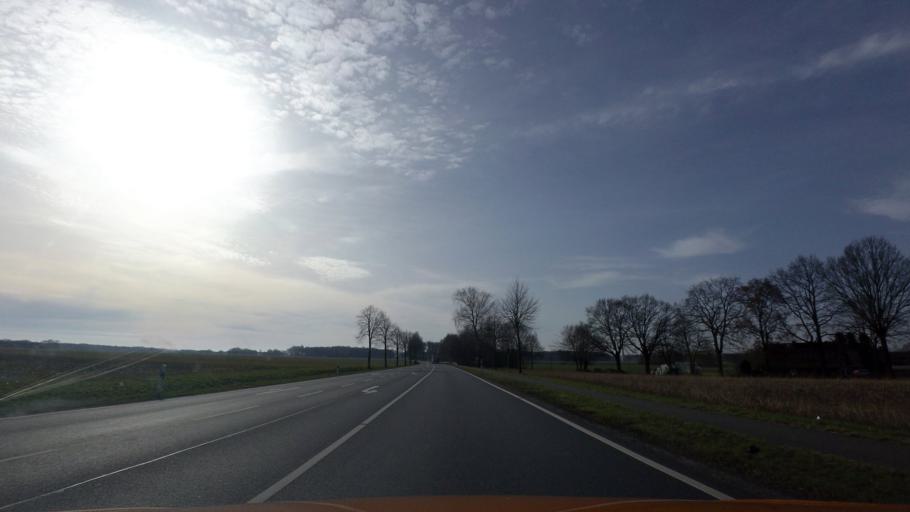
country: DE
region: Lower Saxony
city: Scholen
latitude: 52.7276
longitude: 8.7611
